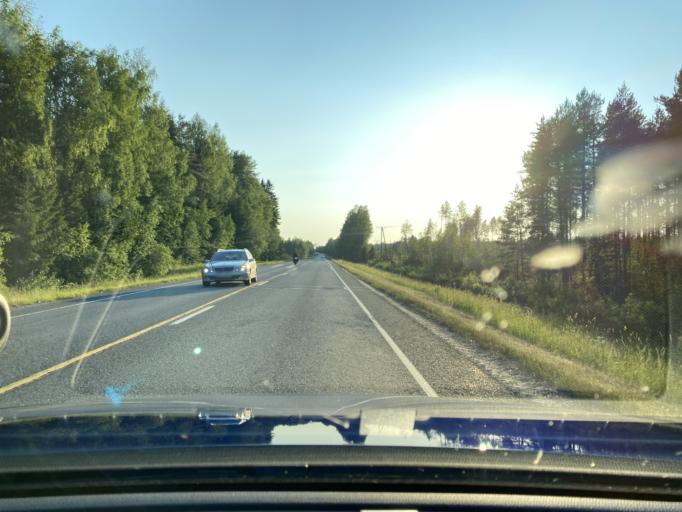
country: FI
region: Haeme
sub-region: Forssa
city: Tammela
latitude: 60.8274
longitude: 23.8972
